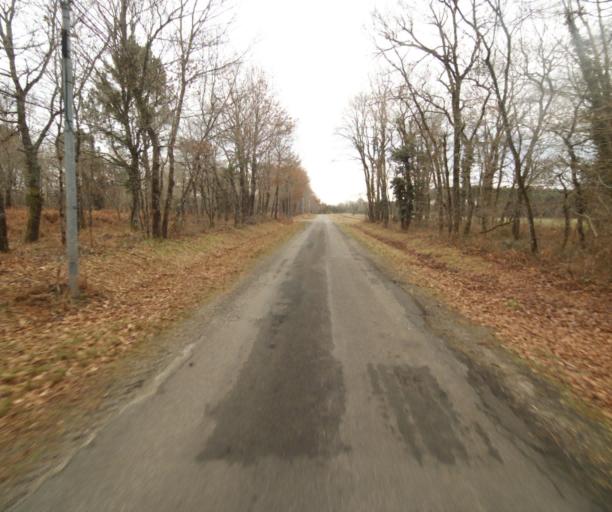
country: FR
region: Aquitaine
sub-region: Departement des Landes
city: Gabarret
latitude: 44.0149
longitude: -0.0504
